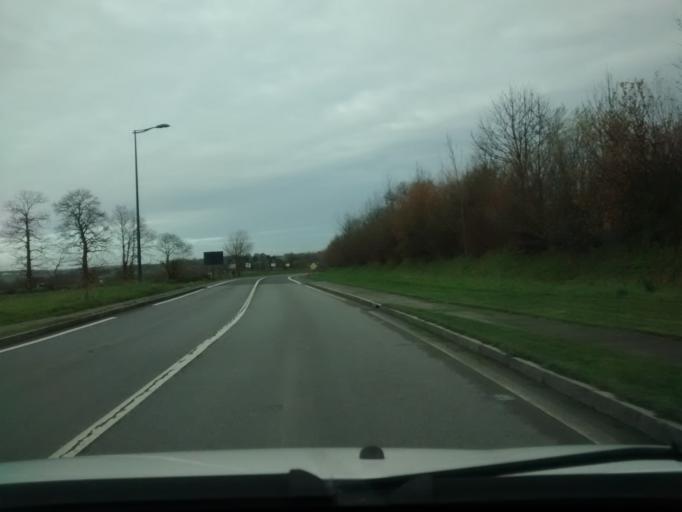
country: FR
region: Brittany
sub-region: Departement d'Ille-et-Vilaine
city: Vitre
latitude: 48.1130
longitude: -1.2246
